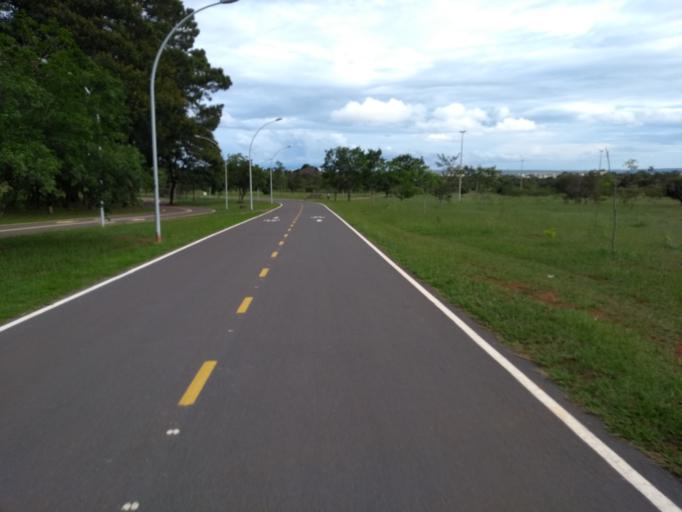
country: BR
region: Federal District
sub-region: Brasilia
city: Brasilia
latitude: -15.8058
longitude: -47.9204
